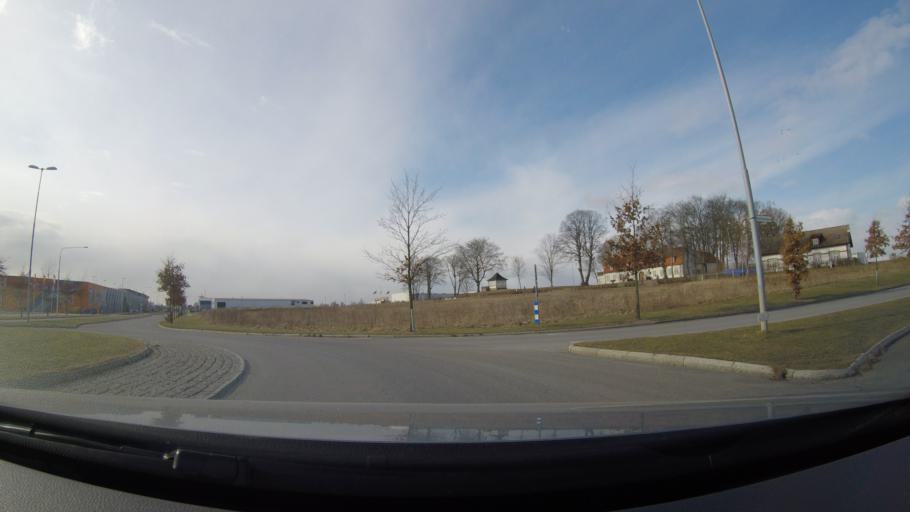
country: SE
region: Skane
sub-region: Burlovs Kommun
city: Arloev
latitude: 55.6129
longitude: 13.1004
